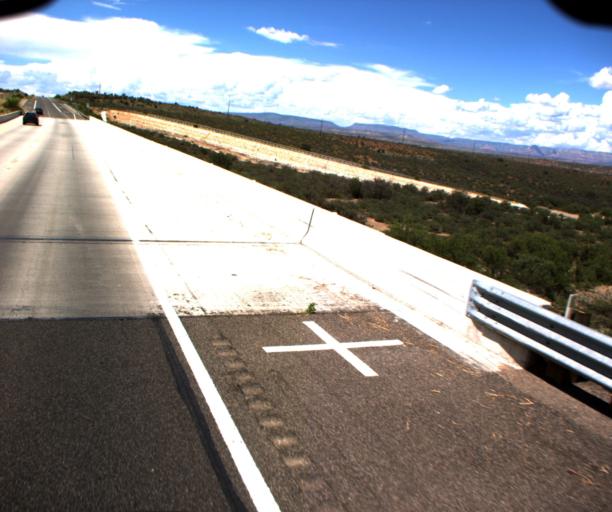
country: US
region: Arizona
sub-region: Yavapai County
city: Verde Village
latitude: 34.6781
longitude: -111.9721
